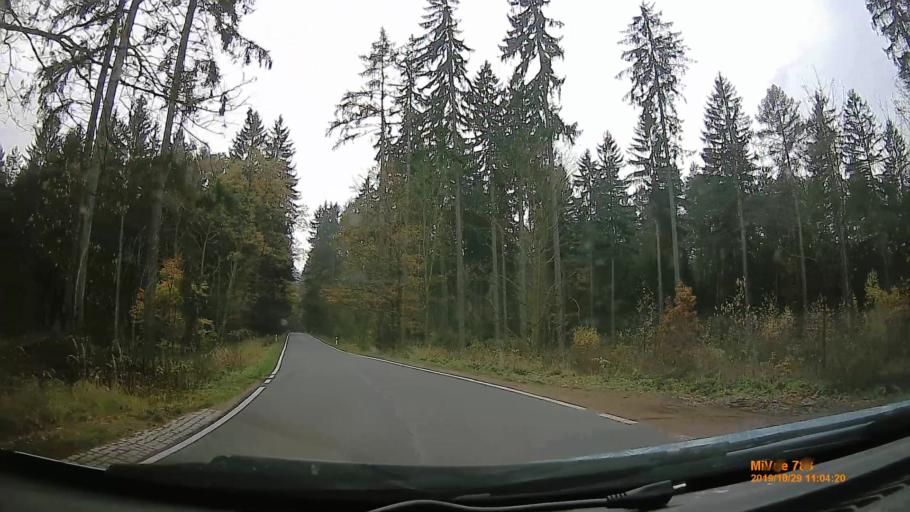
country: PL
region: Lower Silesian Voivodeship
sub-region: Powiat klodzki
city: Szczytna
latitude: 50.4782
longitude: 16.4651
